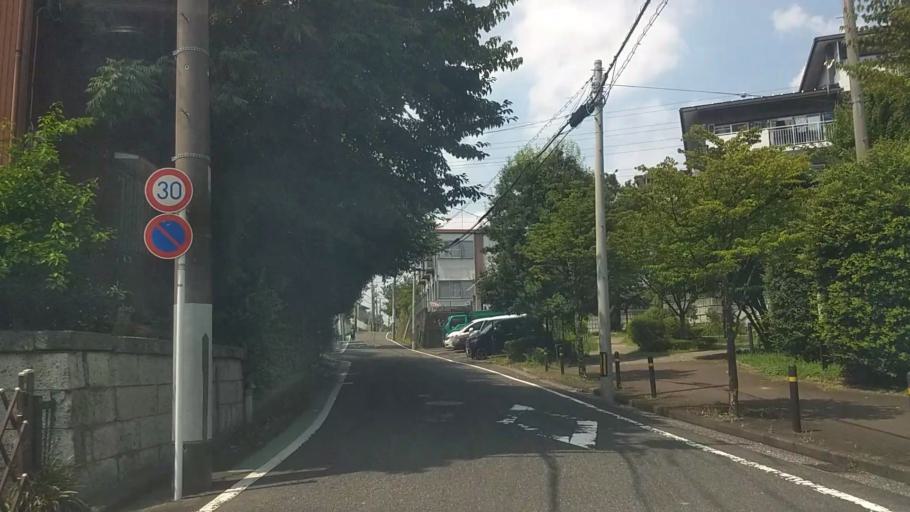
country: JP
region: Kanagawa
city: Yokohama
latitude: 35.4915
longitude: 139.6166
